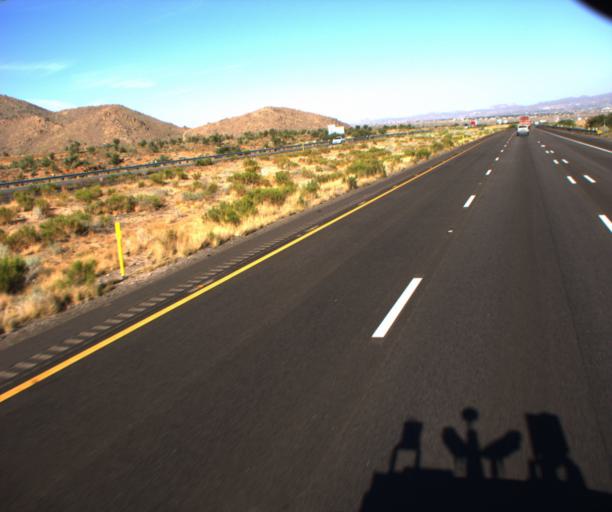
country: US
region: Arizona
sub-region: Mohave County
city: New Kingman-Butler
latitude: 35.1982
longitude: -113.9115
